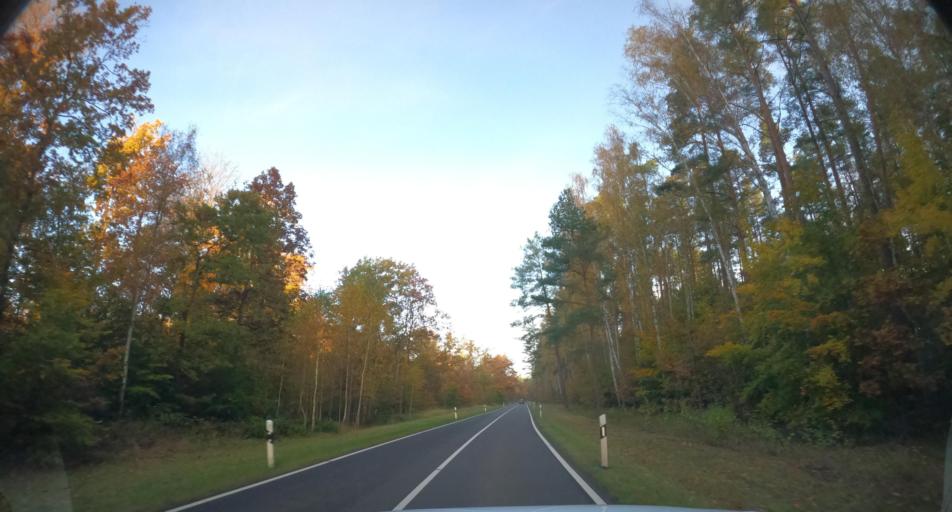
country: DE
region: Mecklenburg-Vorpommern
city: Ahlbeck
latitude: 53.6492
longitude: 14.1908
